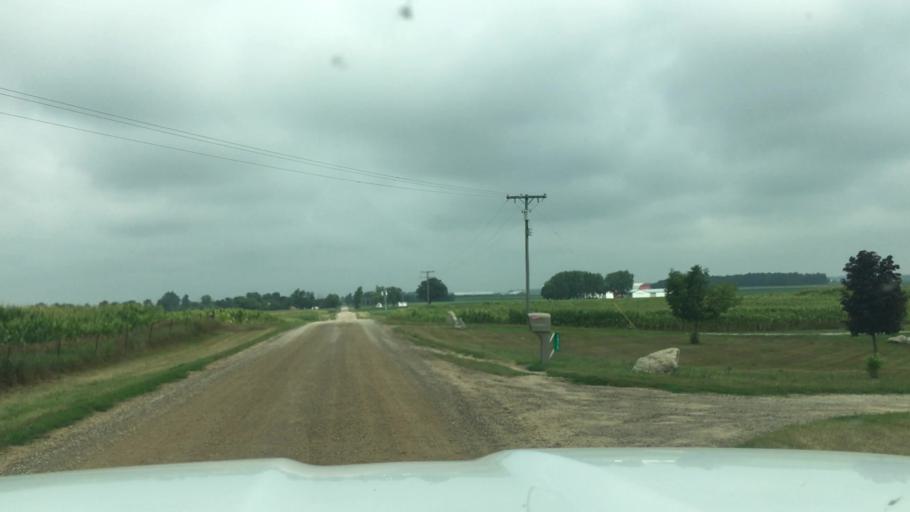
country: US
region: Michigan
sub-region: Sanilac County
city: Marlette
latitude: 43.3313
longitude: -82.9746
